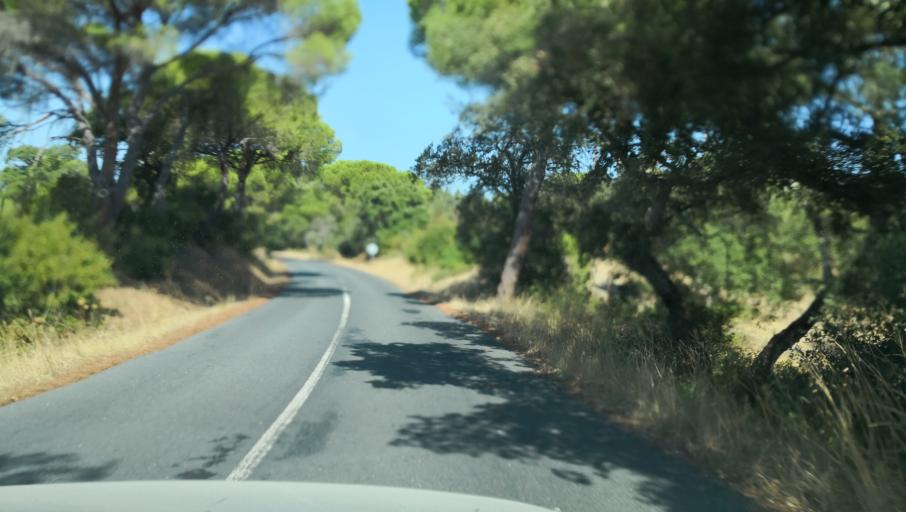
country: PT
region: Setubal
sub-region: Alcacer do Sal
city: Alcacer do Sal
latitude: 38.3004
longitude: -8.4047
